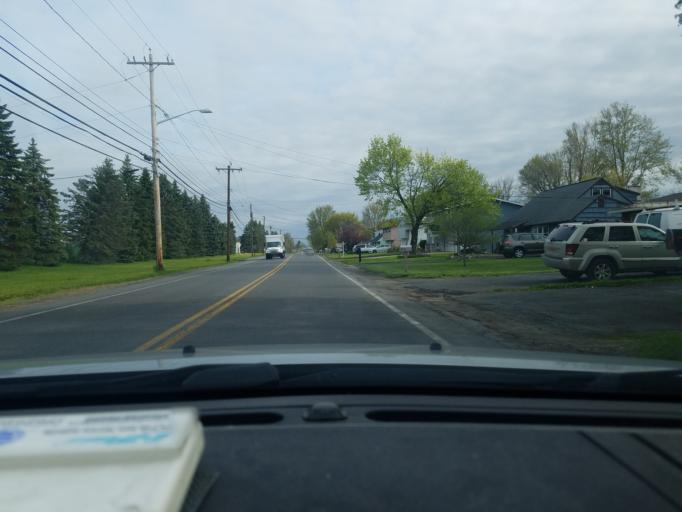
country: US
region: New York
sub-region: Onondaga County
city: East Syracuse
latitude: 43.0807
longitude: -76.0777
